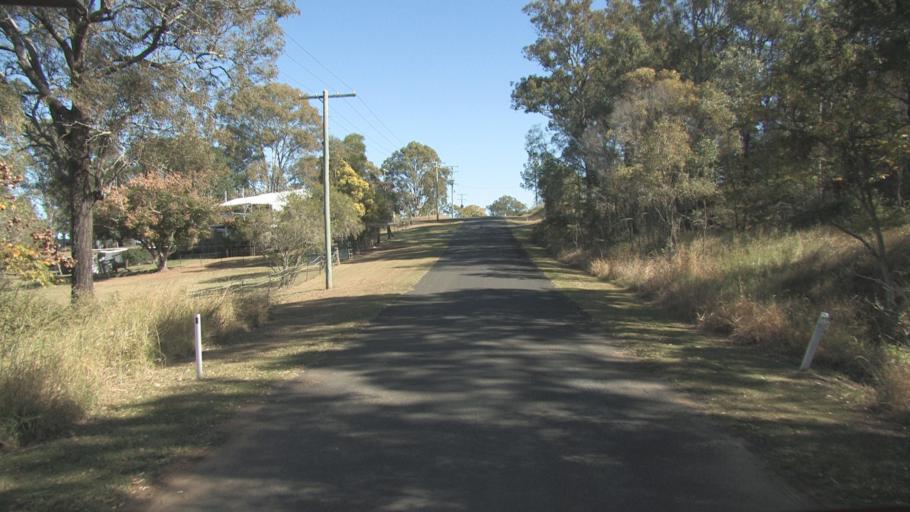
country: AU
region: Queensland
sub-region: Logan
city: Cedar Vale
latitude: -27.8928
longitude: 152.9798
